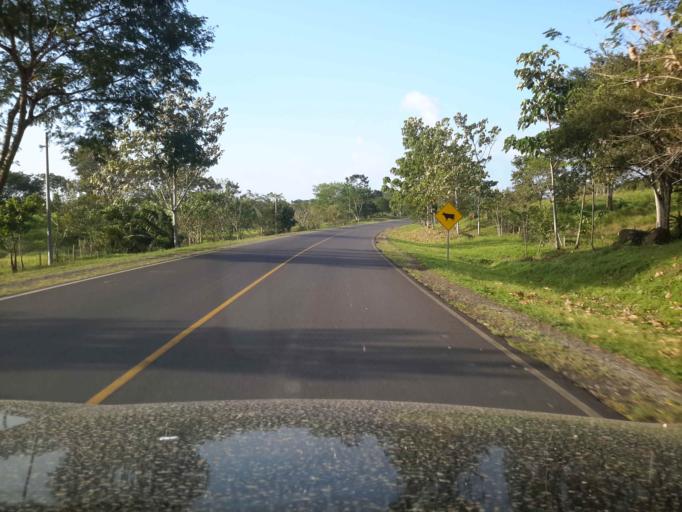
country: NI
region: Rio San Juan
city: San Carlos
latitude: 11.2103
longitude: -84.6866
